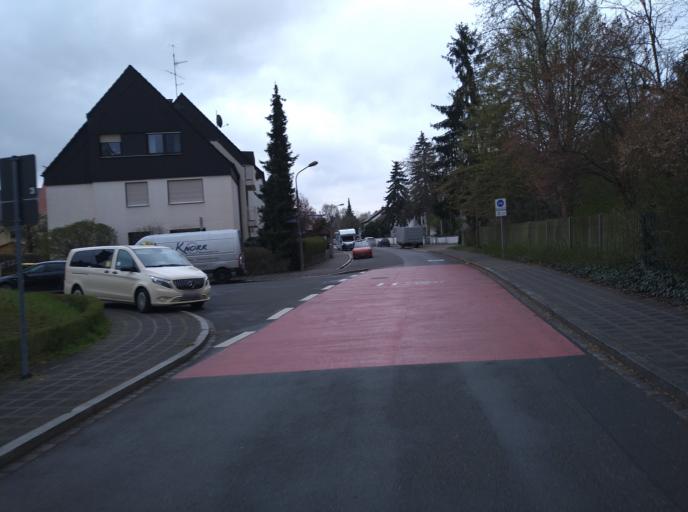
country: DE
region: Bavaria
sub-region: Regierungsbezirk Mittelfranken
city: Nuernberg
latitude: 49.4461
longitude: 11.1182
